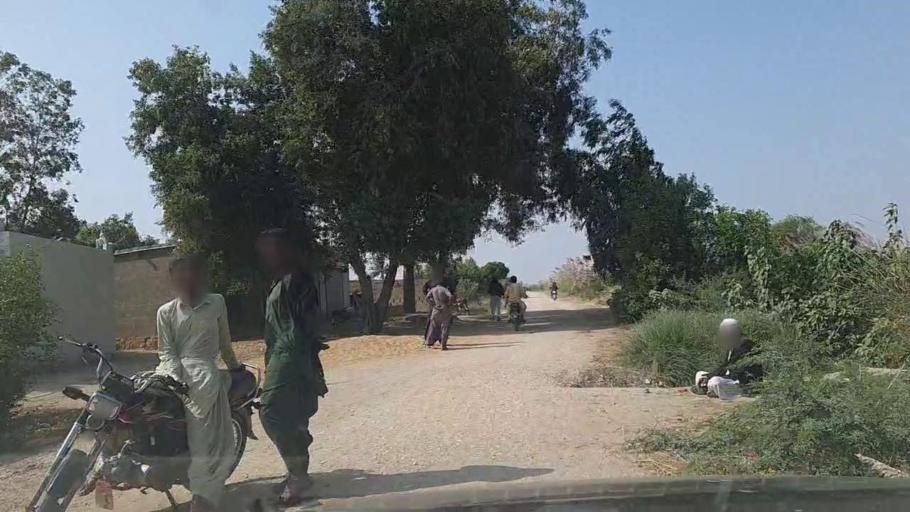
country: PK
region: Sindh
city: Gharo
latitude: 24.7029
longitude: 67.6388
